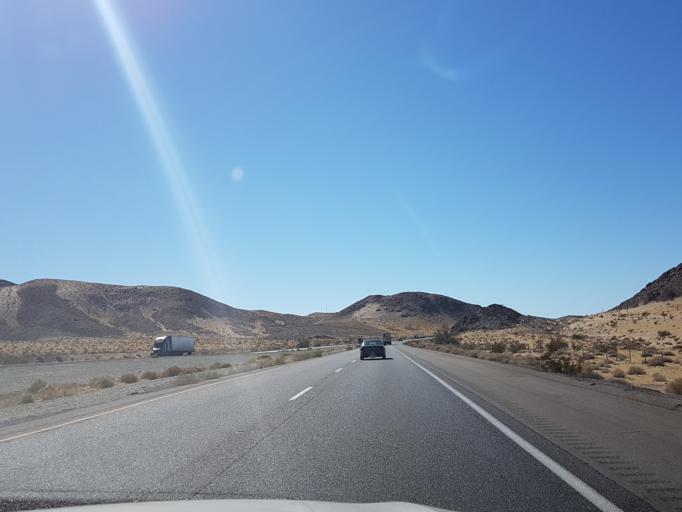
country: US
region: California
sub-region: San Bernardino County
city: Fort Irwin
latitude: 35.0818
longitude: -116.3825
